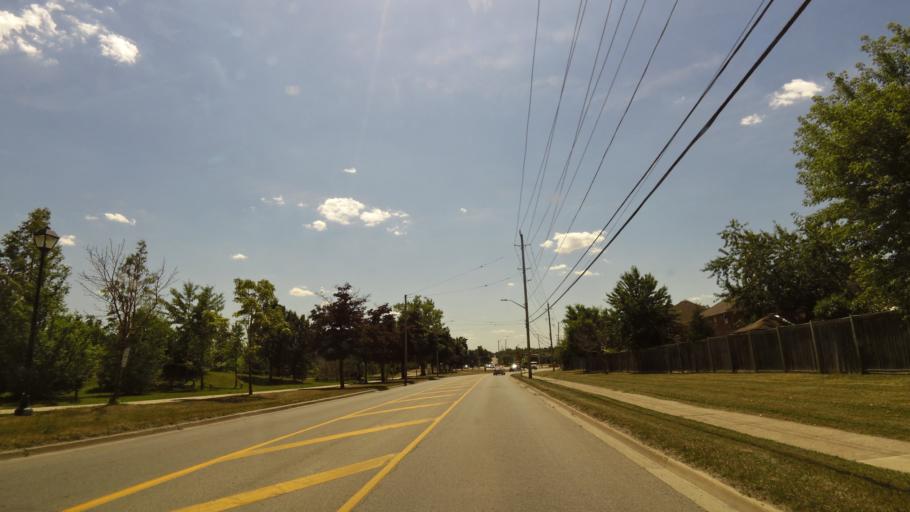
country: CA
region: Ontario
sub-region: Halton
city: Milton
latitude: 43.6525
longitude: -79.9139
